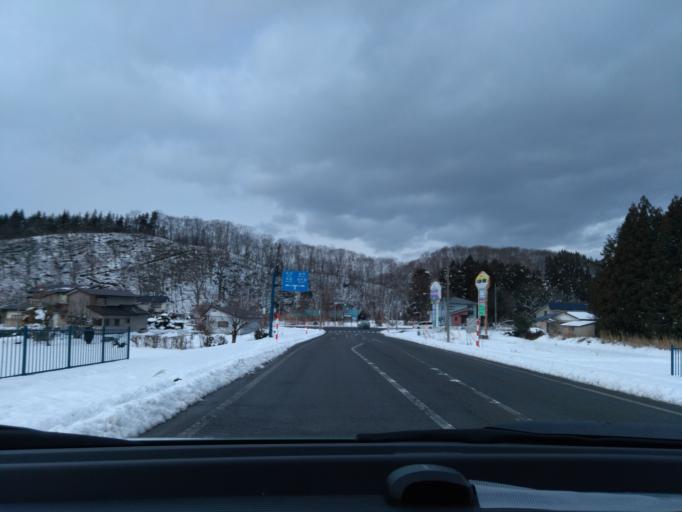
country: JP
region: Akita
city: Kakunodatemachi
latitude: 39.6254
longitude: 140.6285
